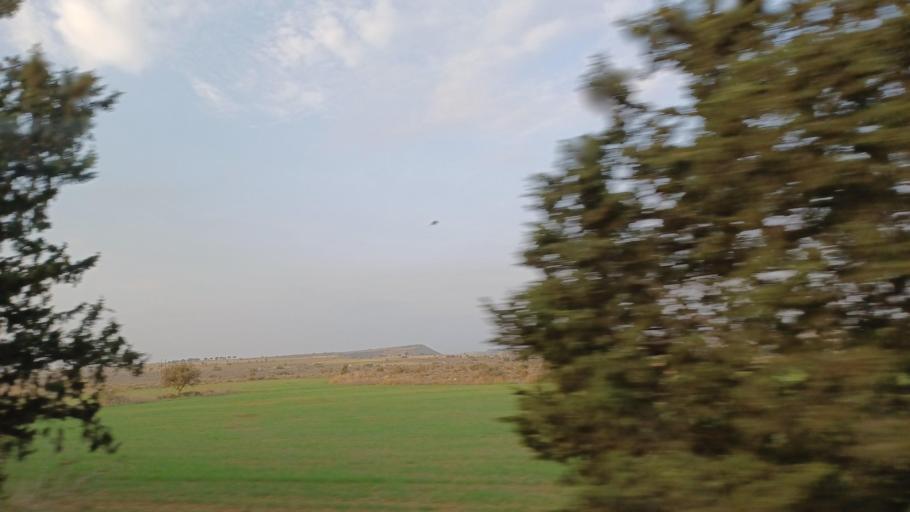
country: CY
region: Lefkosia
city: Lympia
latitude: 35.0172
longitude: 33.4956
